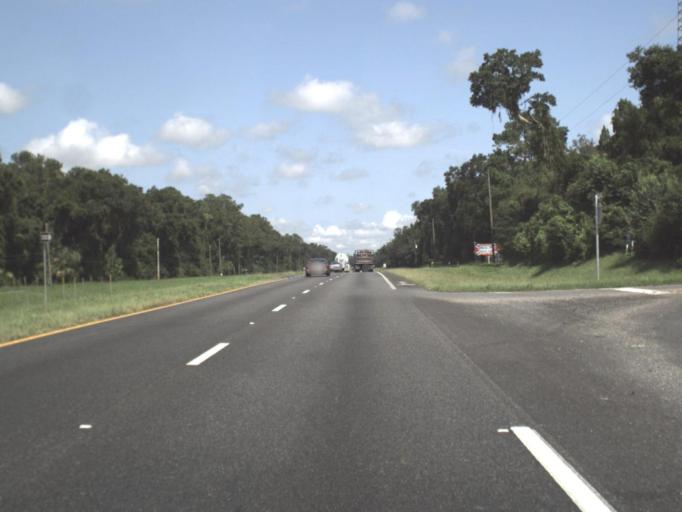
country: US
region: Florida
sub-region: Hernando County
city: Hill 'n Dale
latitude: 28.5306
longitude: -82.3254
